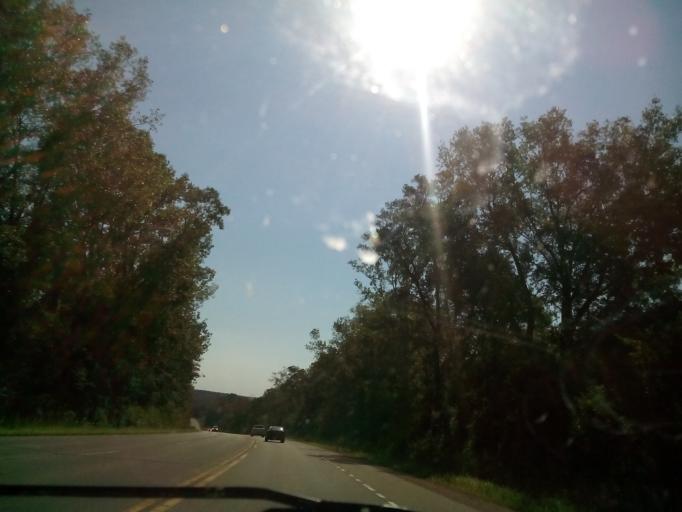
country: US
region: Wisconsin
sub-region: Green County
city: New Glarus
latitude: 42.8653
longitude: -89.6064
